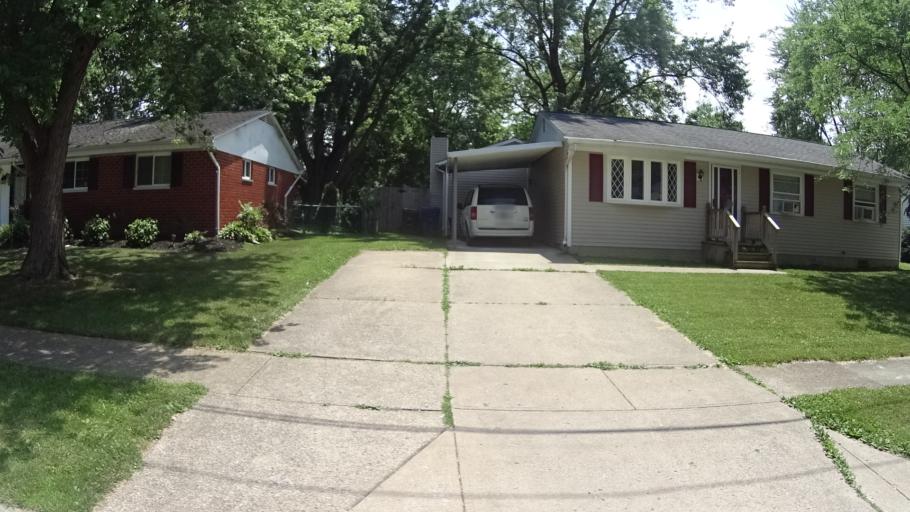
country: US
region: Ohio
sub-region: Lorain County
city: Vermilion
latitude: 41.4070
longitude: -82.3532
